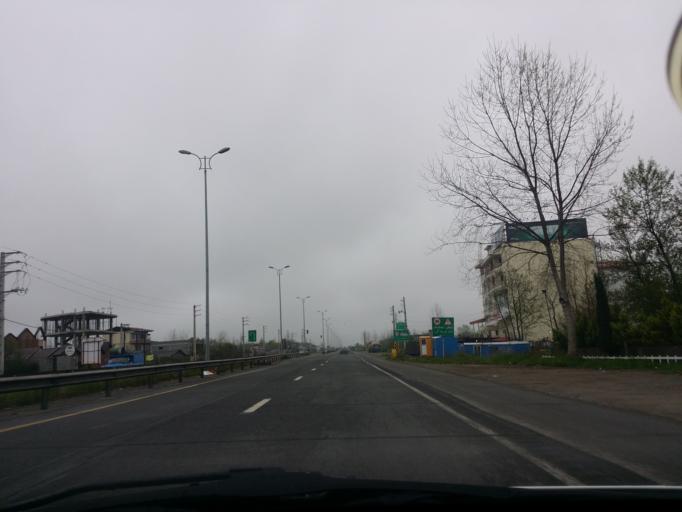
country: IR
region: Mazandaran
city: Tonekabon
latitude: 36.8024
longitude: 50.8830
